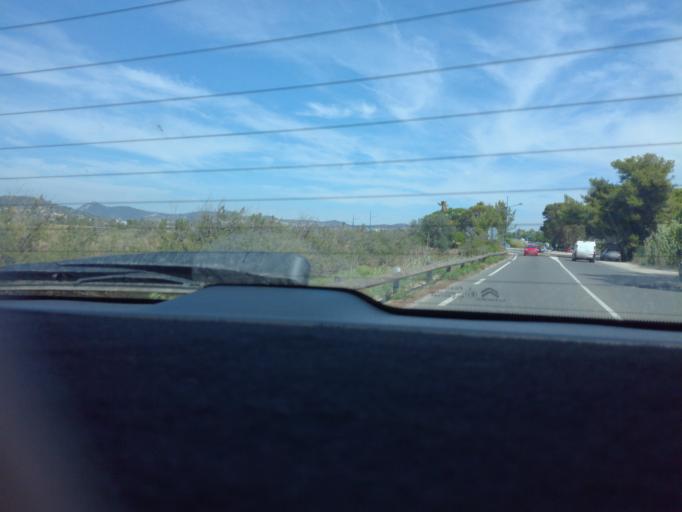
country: FR
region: Provence-Alpes-Cote d'Azur
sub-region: Departement du Var
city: Hyeres
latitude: 43.0791
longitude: 6.1494
